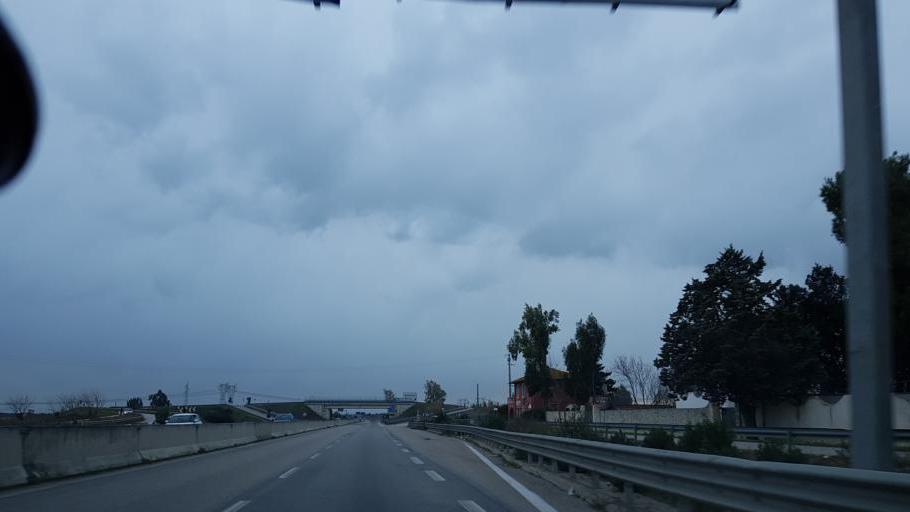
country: IT
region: Apulia
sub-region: Provincia di Brindisi
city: Brindisi
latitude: 40.6061
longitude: 17.8856
